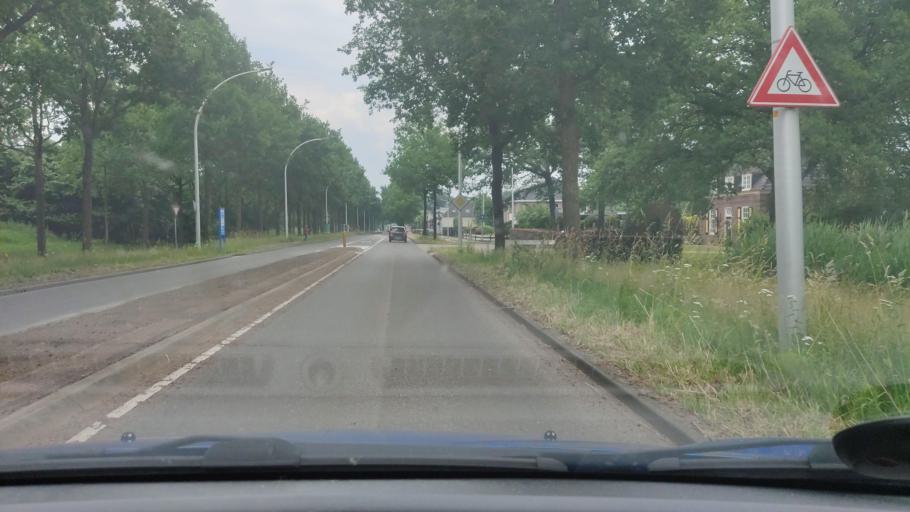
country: NL
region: Overijssel
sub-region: Gemeente Almelo
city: Almelo
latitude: 52.3557
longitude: 6.6387
